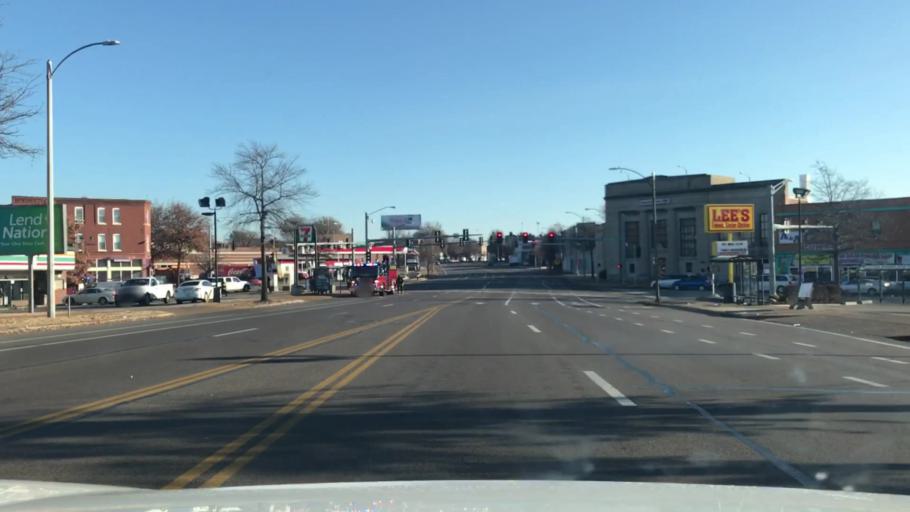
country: US
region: Missouri
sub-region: City of Saint Louis
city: St. Louis
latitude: 38.6045
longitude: -90.2240
